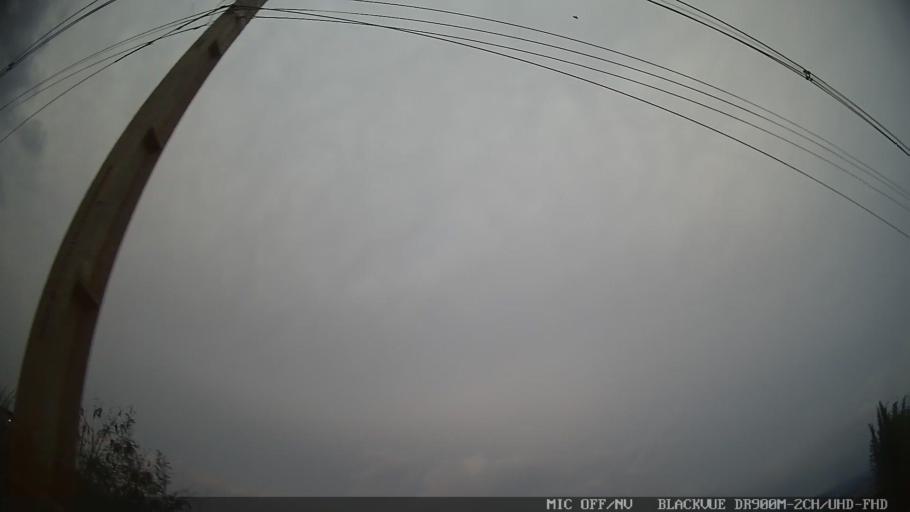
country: BR
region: Sao Paulo
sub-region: Braganca Paulista
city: Braganca Paulista
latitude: -22.9498
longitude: -46.5701
